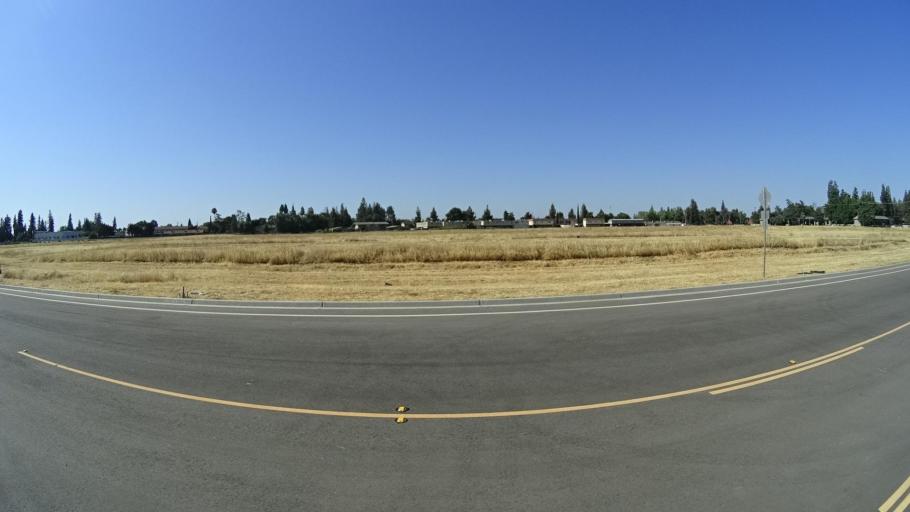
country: US
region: California
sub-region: Fresno County
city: Sunnyside
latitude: 36.7435
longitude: -119.6975
